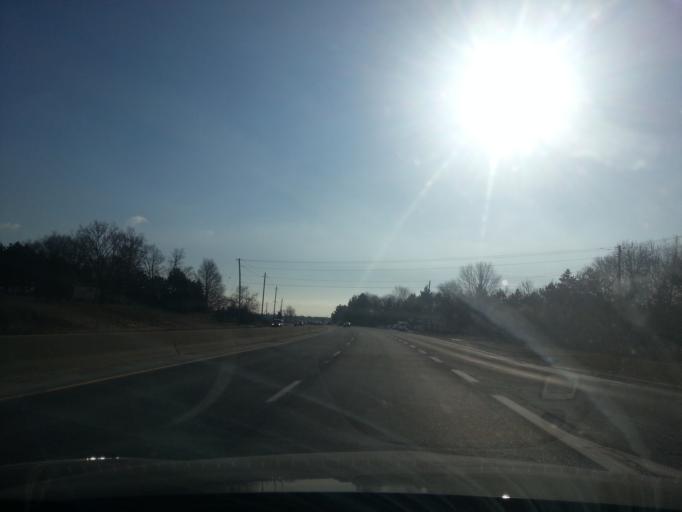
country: CA
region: Ontario
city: Oshawa
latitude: 43.9642
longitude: -78.6111
